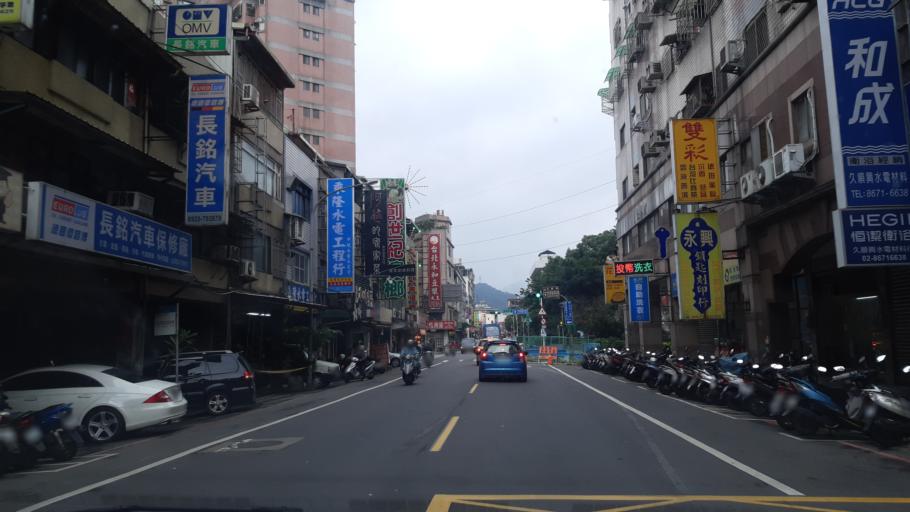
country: TW
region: Taiwan
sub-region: Taoyuan
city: Taoyuan
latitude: 24.9361
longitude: 121.3653
